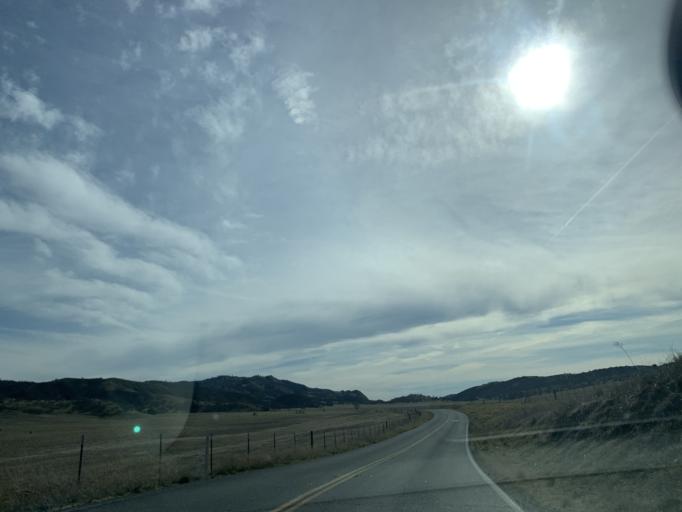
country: US
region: California
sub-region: Monterey County
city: Greenfield
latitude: 36.4899
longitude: -121.0764
